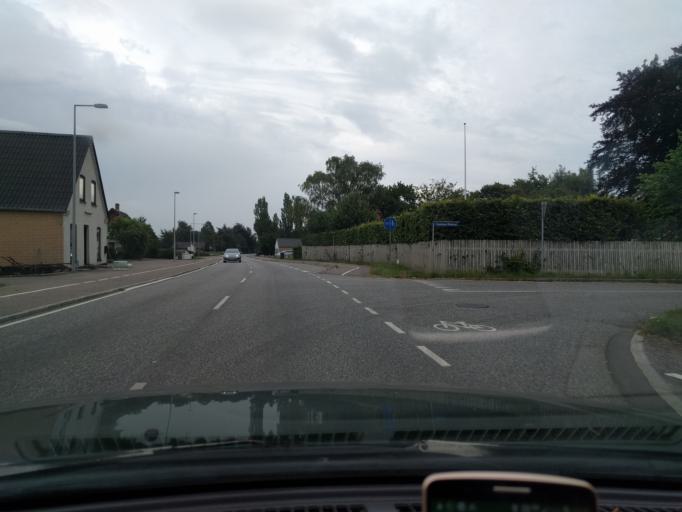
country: DK
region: Zealand
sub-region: Slagelse Kommune
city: Skaelskor
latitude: 55.2389
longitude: 11.4252
